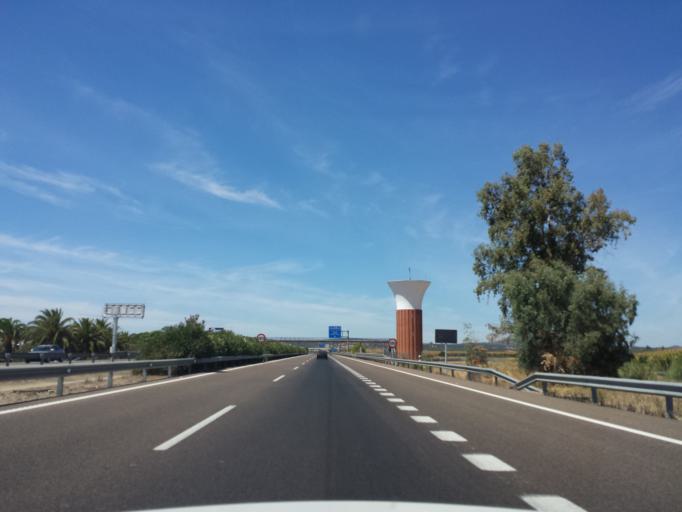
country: ES
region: Extremadura
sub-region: Provincia de Badajoz
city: Valdetorres
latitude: 38.9910
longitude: -6.1101
